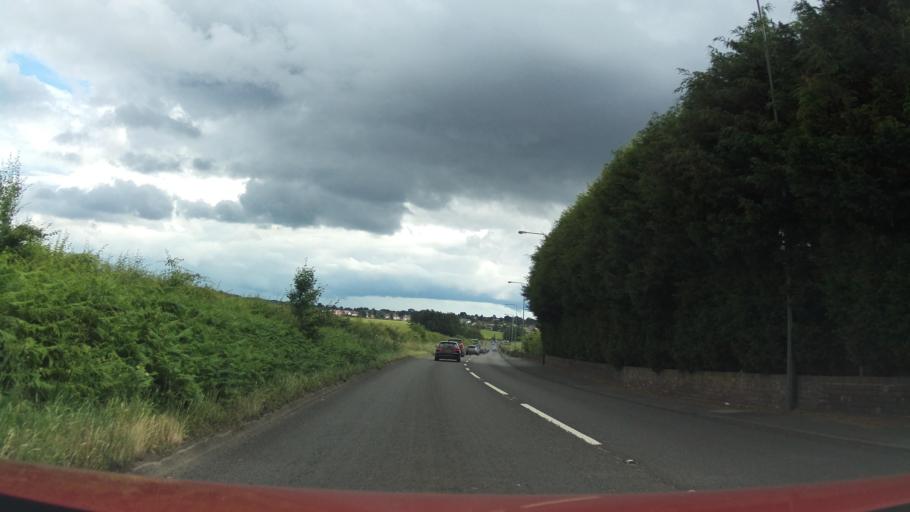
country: GB
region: England
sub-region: Worcestershire
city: Kidderminster
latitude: 52.4117
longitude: -2.2272
